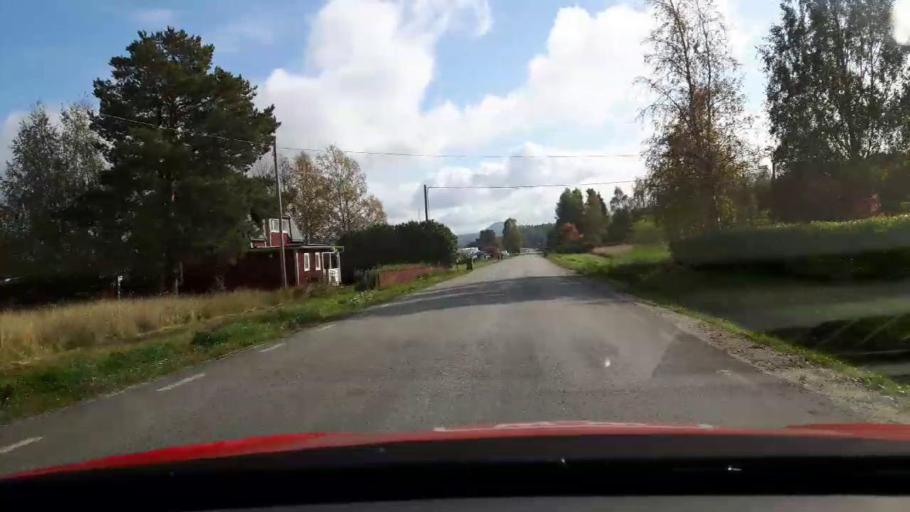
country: SE
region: Gaevleborg
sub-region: Ljusdals Kommun
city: Jaervsoe
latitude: 61.7553
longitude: 16.1229
